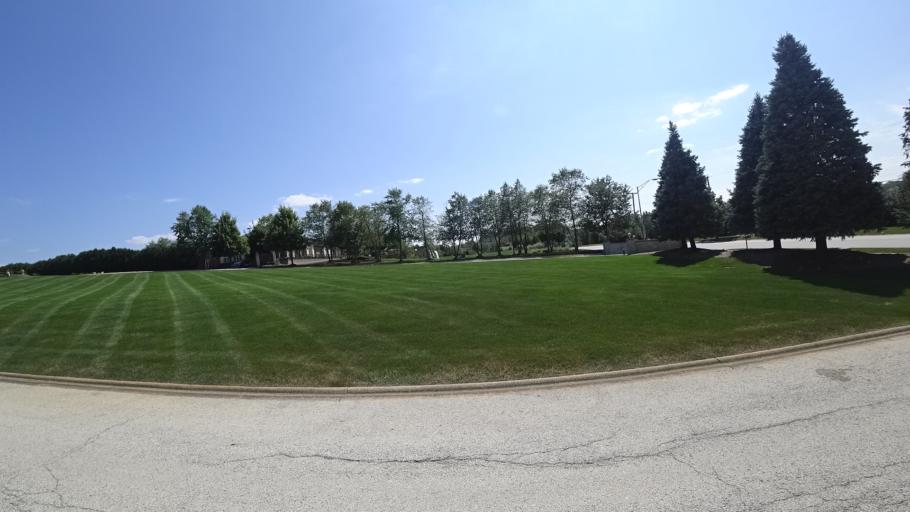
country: US
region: Illinois
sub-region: Cook County
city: Orland Park
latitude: 41.6312
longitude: -87.8825
